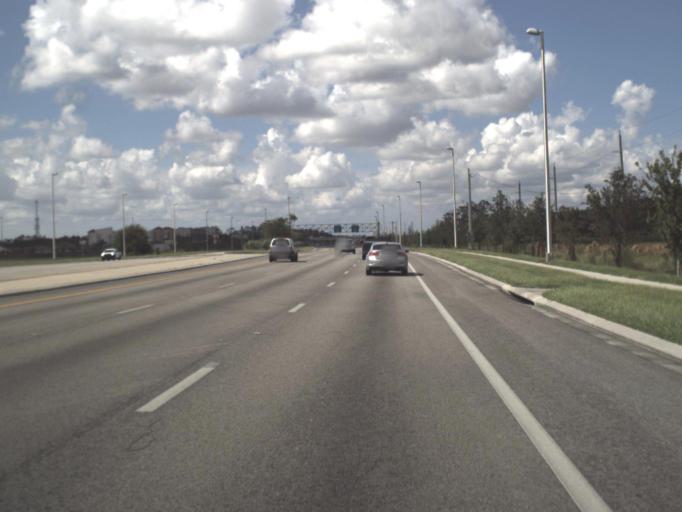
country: US
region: Florida
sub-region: Lee County
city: Tice
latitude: 26.6323
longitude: -81.7934
